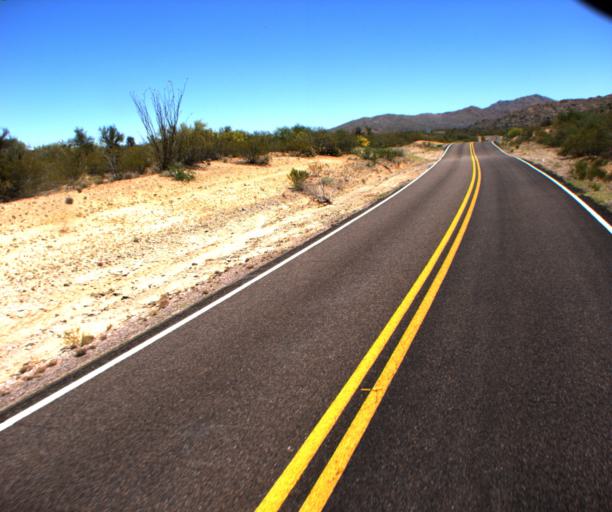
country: US
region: Arizona
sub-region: Yavapai County
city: Bagdad
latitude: 34.4798
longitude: -113.2030
